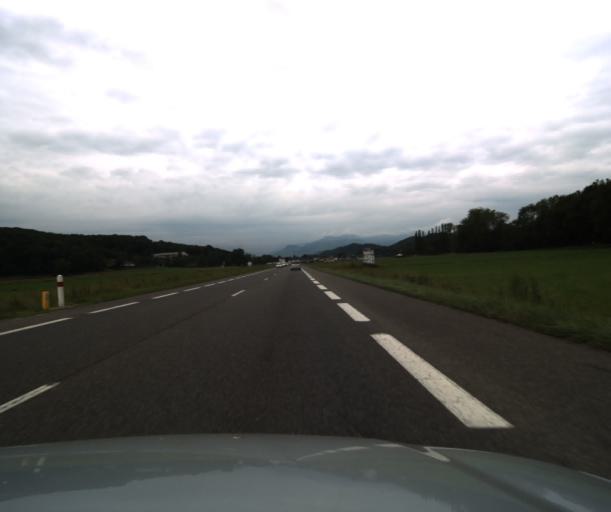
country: FR
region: Midi-Pyrenees
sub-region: Departement des Hautes-Pyrenees
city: Ossun
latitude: 43.1492
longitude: -0.0234
